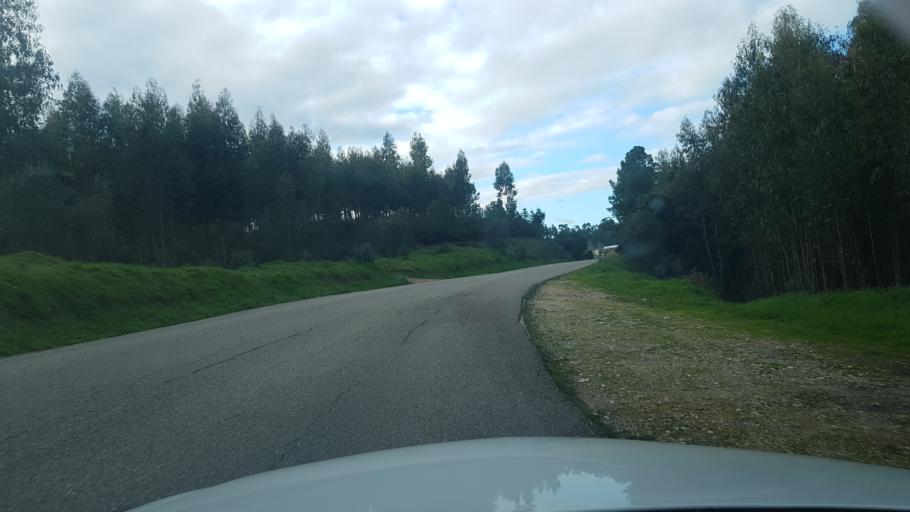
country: PT
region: Santarem
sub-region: Constancia
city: Constancia
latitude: 39.4796
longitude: -8.3503
